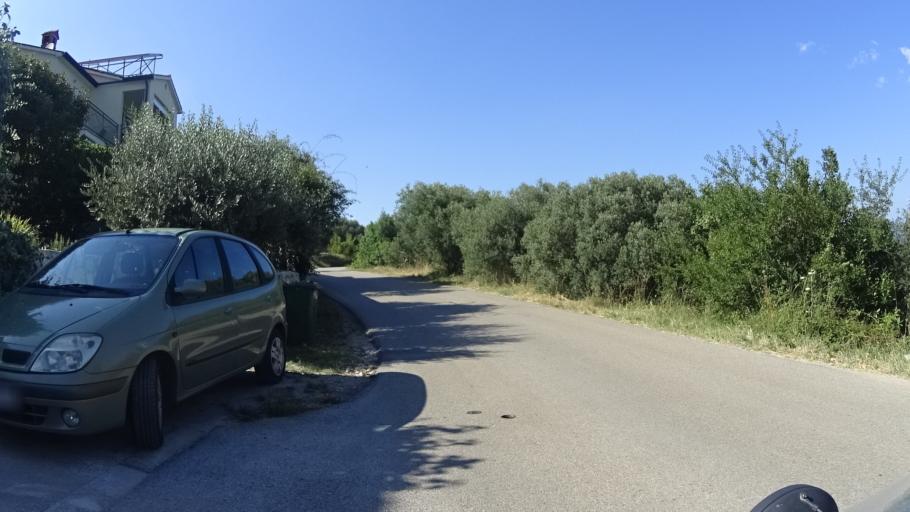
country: HR
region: Istarska
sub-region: Grad Labin
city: Rabac
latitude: 45.0023
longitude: 14.1631
